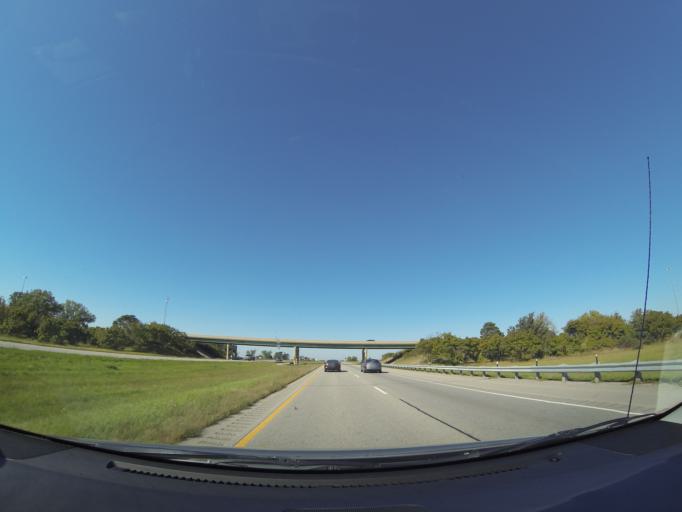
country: US
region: Nebraska
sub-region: Seward County
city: Milford
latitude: 40.8223
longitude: -97.1006
